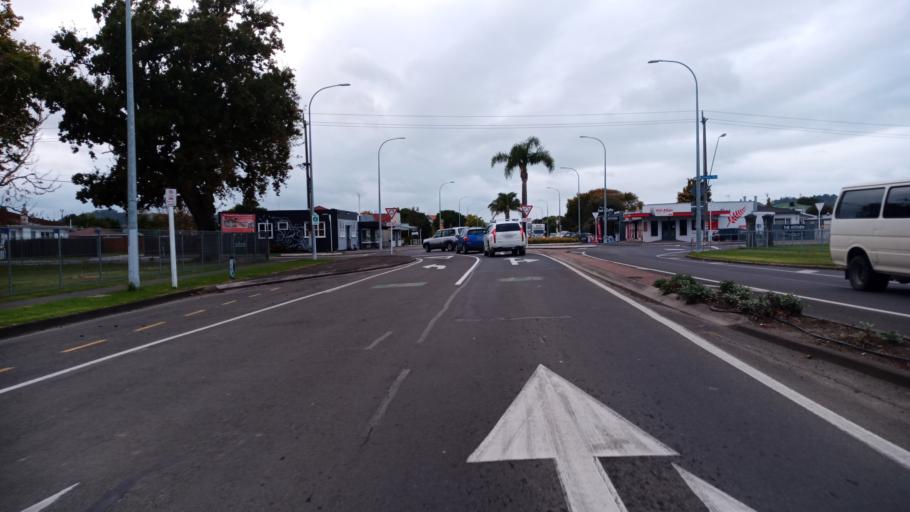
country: NZ
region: Gisborne
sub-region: Gisborne District
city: Gisborne
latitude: -38.6557
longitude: 178.0091
